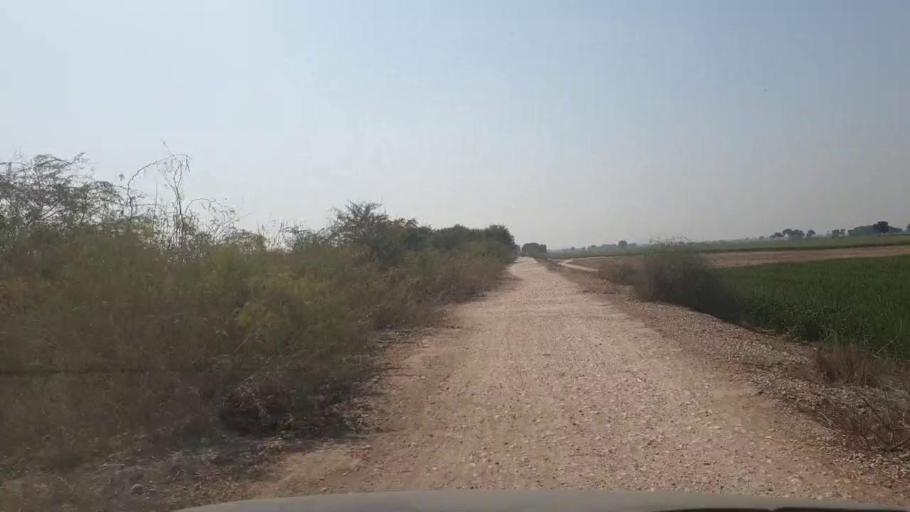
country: PK
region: Sindh
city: Chambar
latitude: 25.2385
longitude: 68.8261
